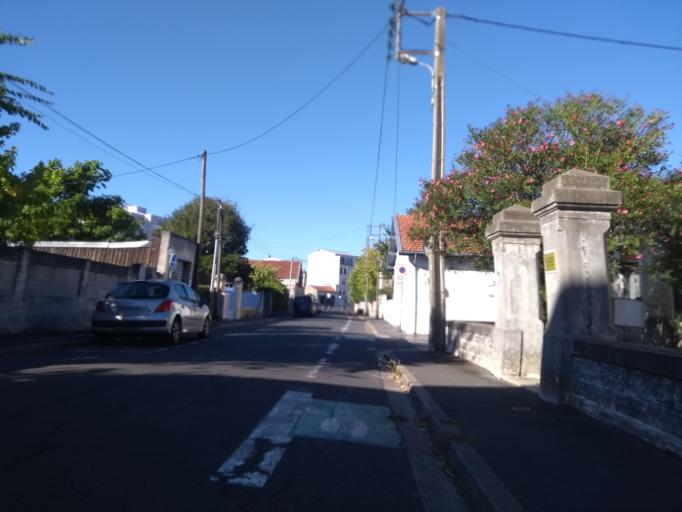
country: FR
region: Aquitaine
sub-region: Departement de la Gironde
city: Talence
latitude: 44.8141
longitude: -0.5869
